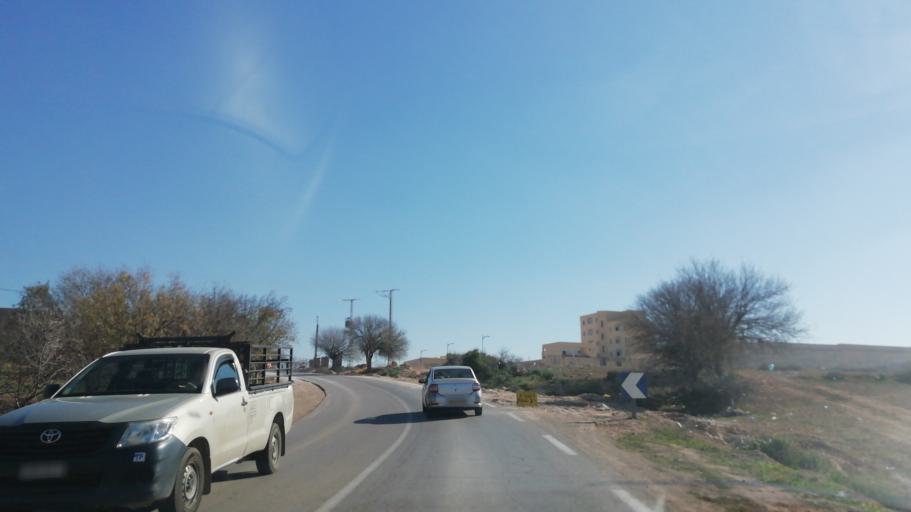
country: DZ
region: Tlemcen
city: Nedroma
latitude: 34.8338
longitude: -1.6837
